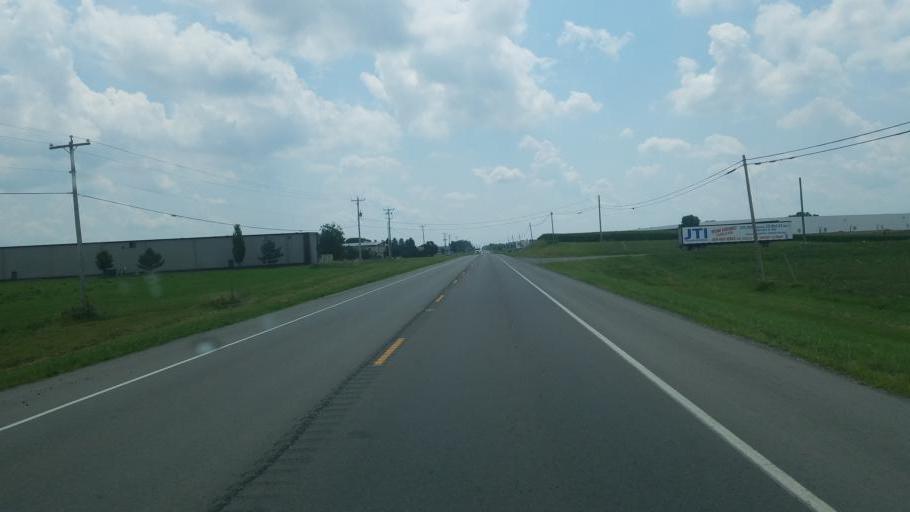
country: US
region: Ohio
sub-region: Hardin County
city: Kenton
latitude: 40.6179
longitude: -83.6246
